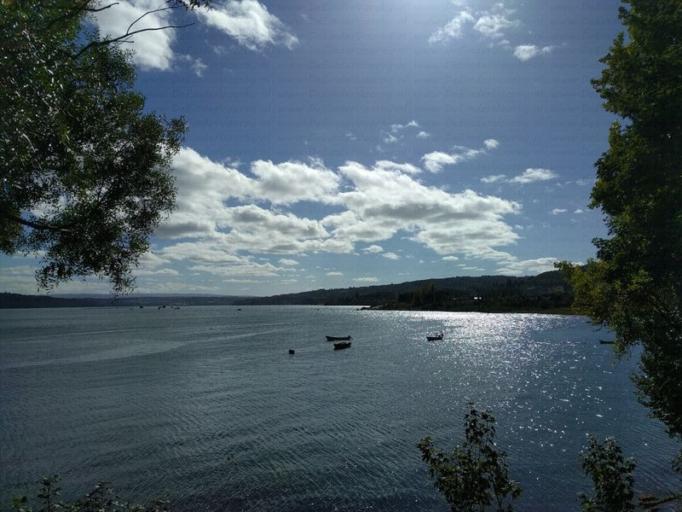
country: CL
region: Los Lagos
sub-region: Provincia de Chiloe
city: Castro
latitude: -42.4396
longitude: -73.6035
